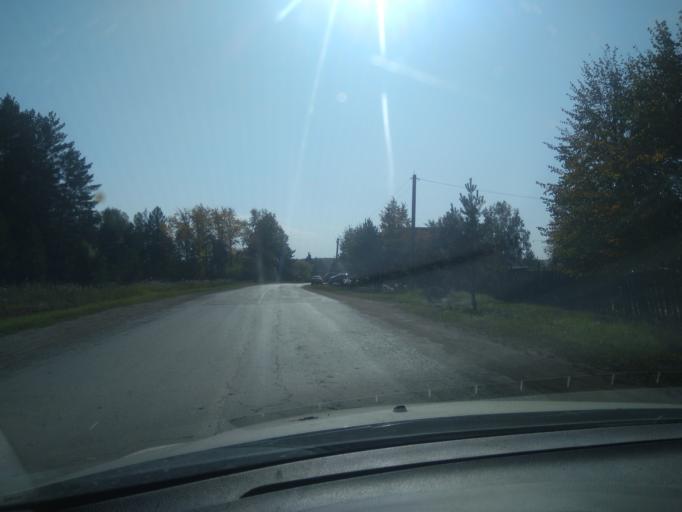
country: RU
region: Sverdlovsk
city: Pokrovskoye
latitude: 56.4439
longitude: 61.6029
